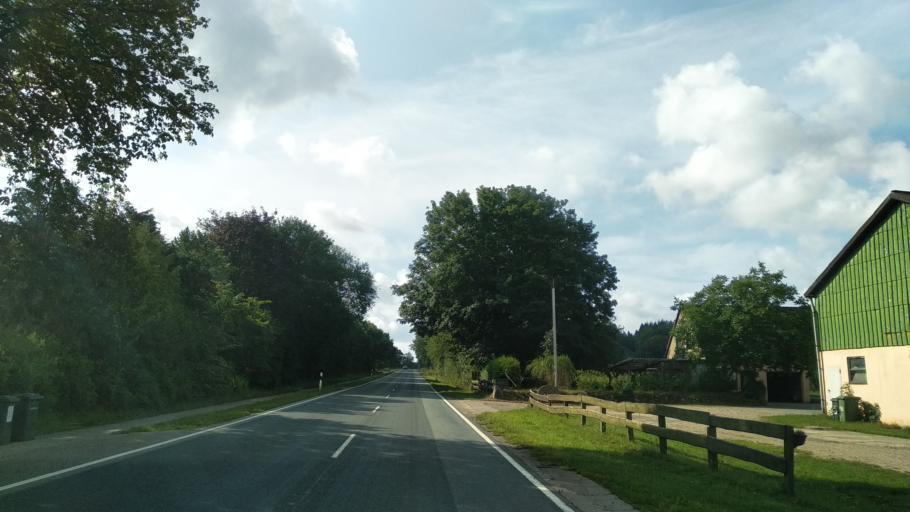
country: DE
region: Schleswig-Holstein
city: Selk
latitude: 54.4827
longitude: 9.5648
